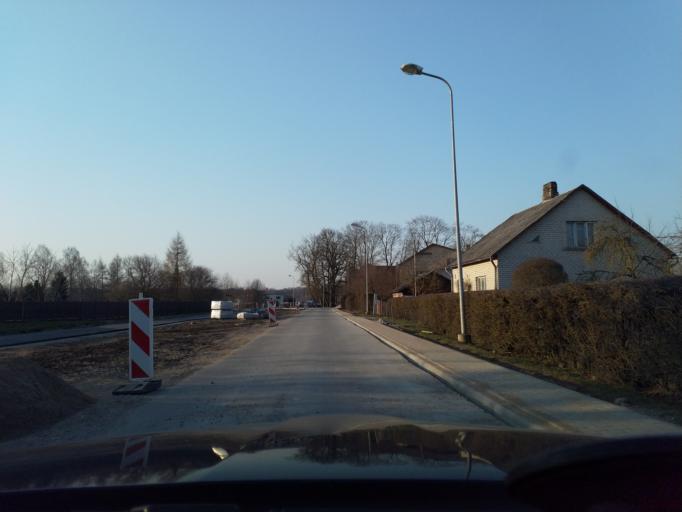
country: LV
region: Grobina
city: Grobina
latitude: 56.5319
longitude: 21.1825
